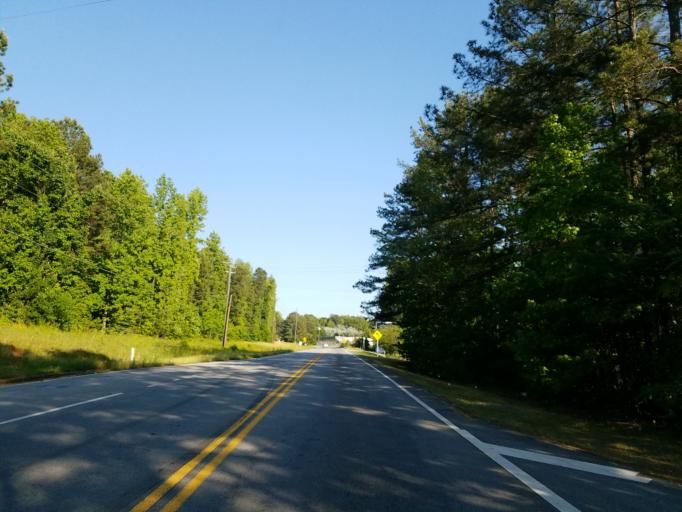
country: US
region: Georgia
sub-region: Carroll County
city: Villa Rica
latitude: 33.7280
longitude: -84.8334
